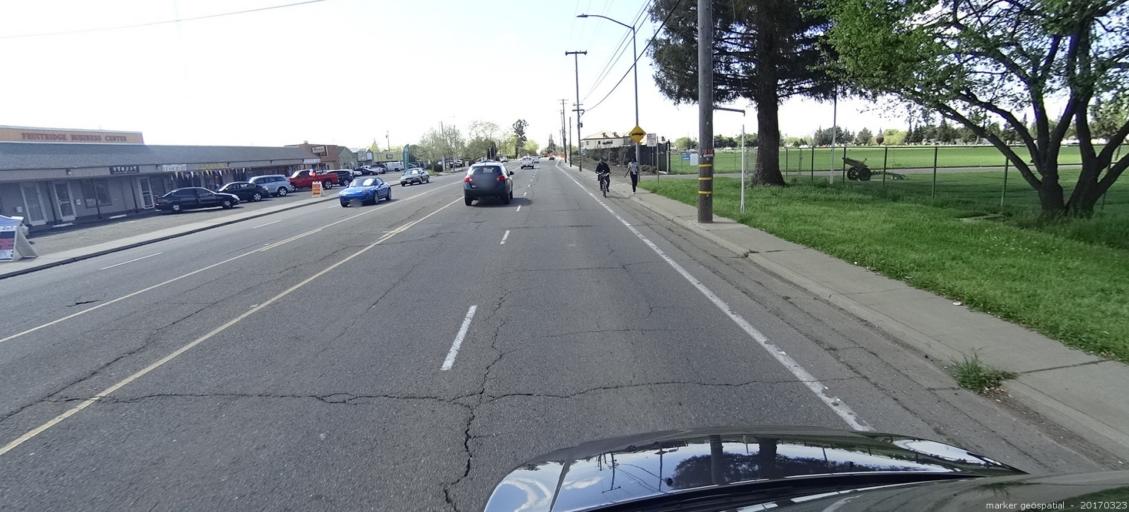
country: US
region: California
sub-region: Sacramento County
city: Florin
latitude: 38.5251
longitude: -121.4234
